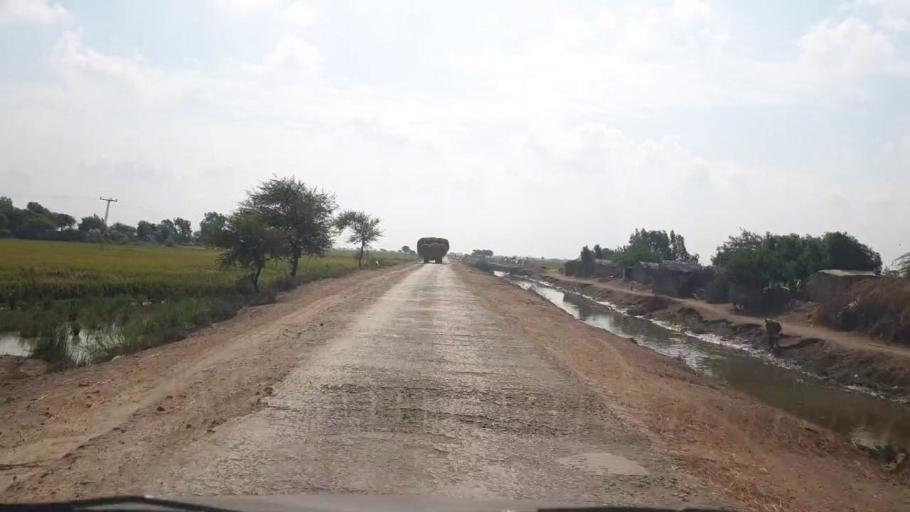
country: PK
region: Sindh
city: Kario
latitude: 24.5895
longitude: 68.5737
